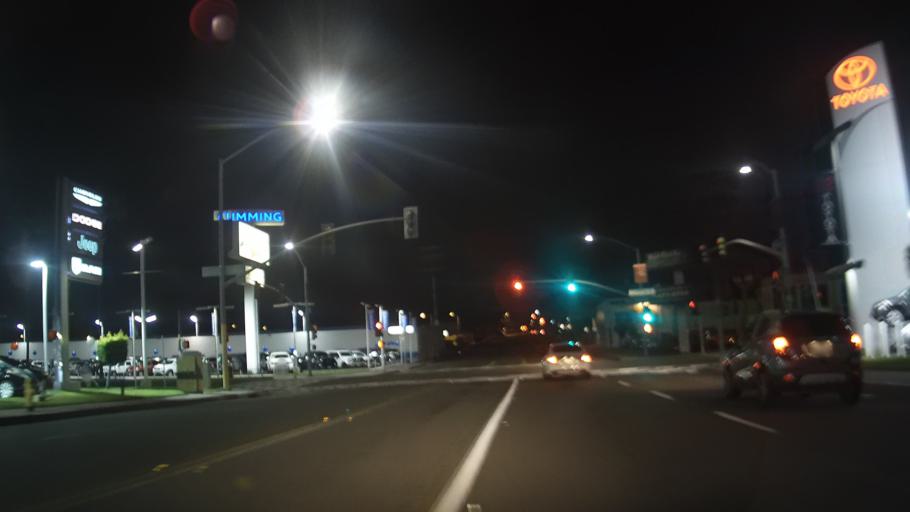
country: US
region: California
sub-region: San Diego County
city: National City
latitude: 32.6619
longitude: -117.1020
